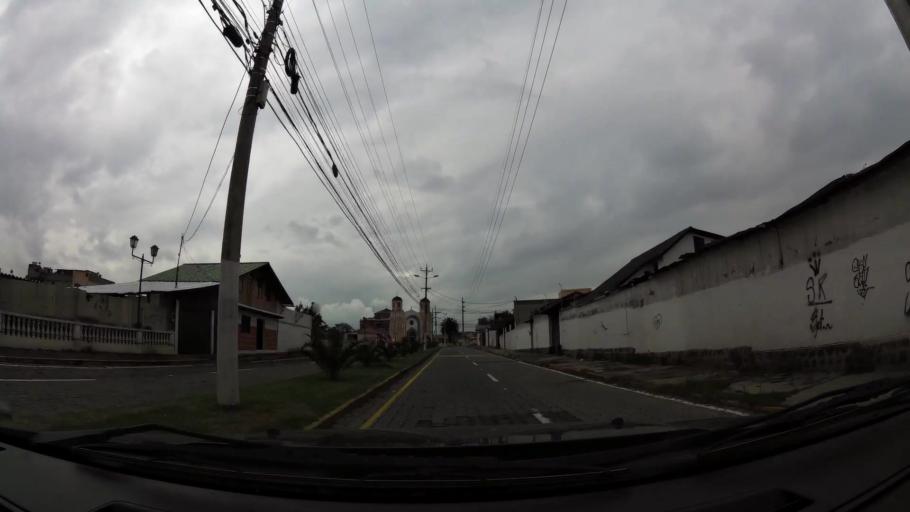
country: EC
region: Pichincha
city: Sangolqui
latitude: -0.3068
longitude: -78.4567
